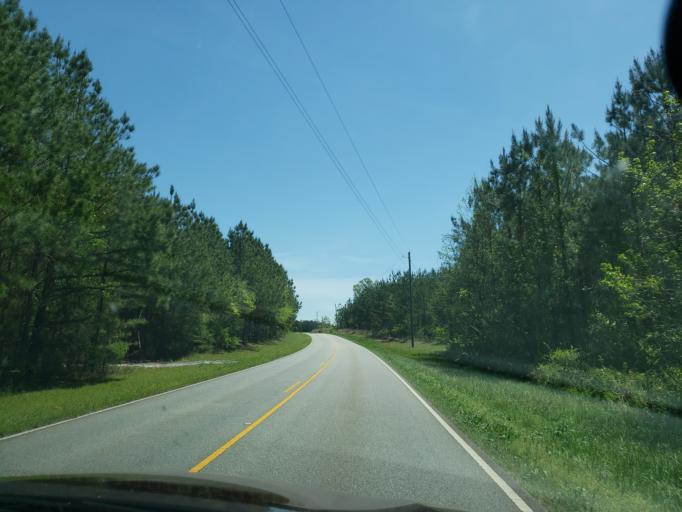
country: US
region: Alabama
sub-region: Tallapoosa County
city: Camp Hill
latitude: 32.7020
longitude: -85.7020
